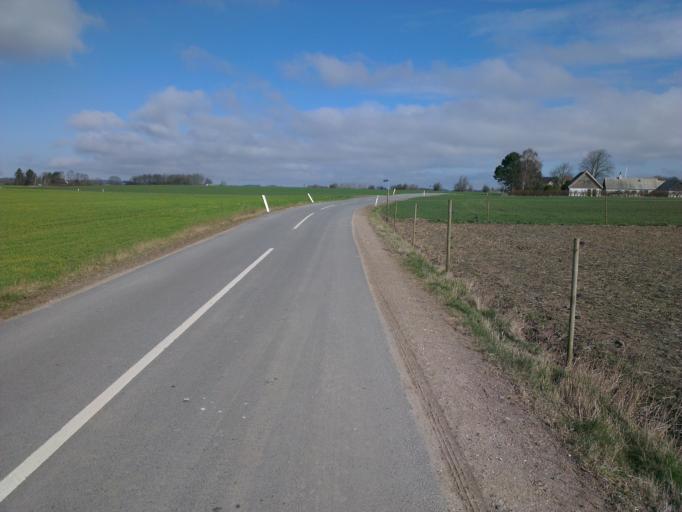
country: DK
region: Capital Region
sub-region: Hillerod Kommune
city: Skaevinge
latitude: 55.8692
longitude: 12.1151
